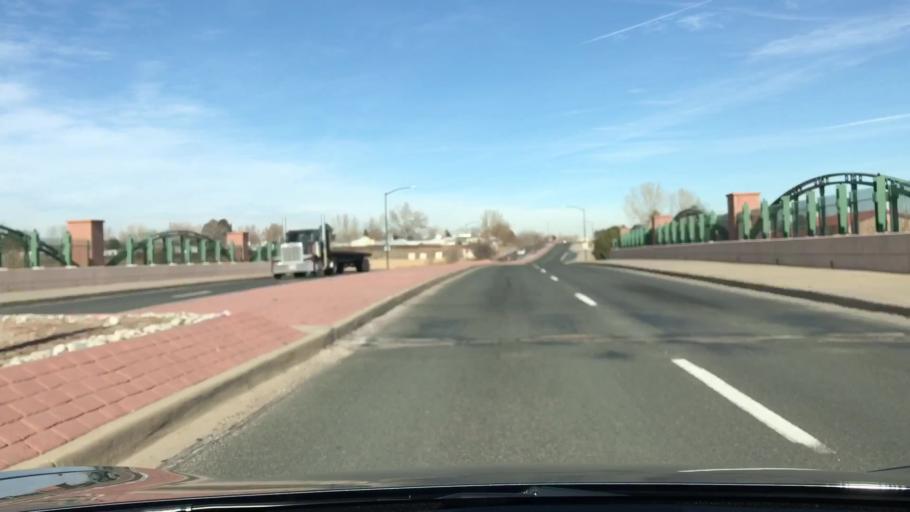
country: US
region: Colorado
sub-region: Adams County
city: Northglenn
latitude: 39.9335
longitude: -104.9970
